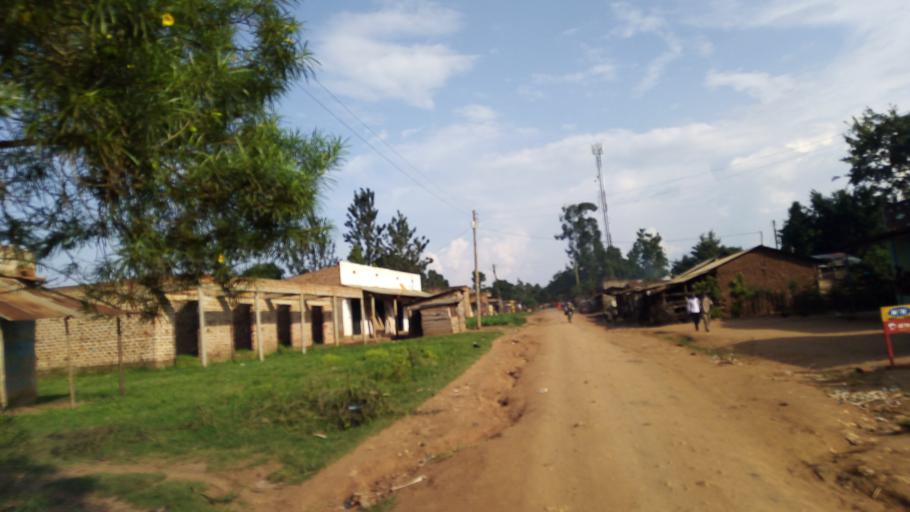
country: UG
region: Eastern Region
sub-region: Mbale District
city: Mbale
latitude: 1.0631
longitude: 34.1542
